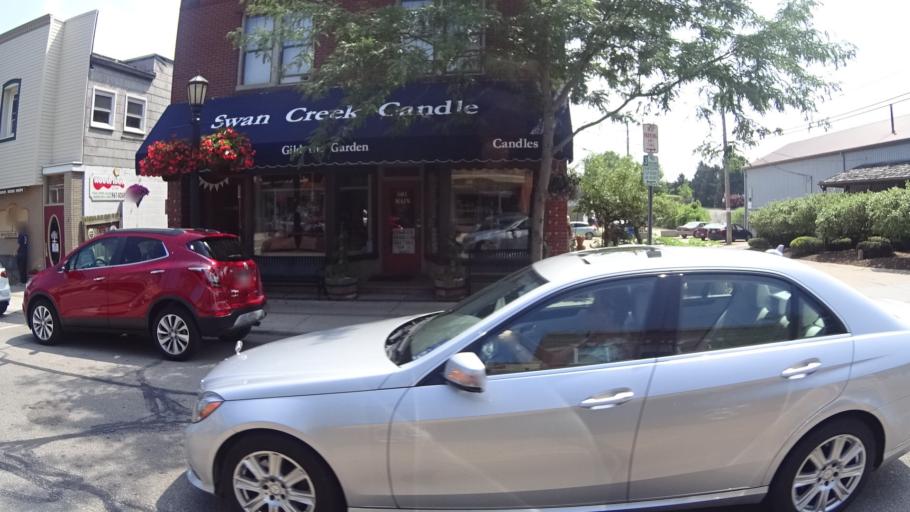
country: US
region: Ohio
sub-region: Lorain County
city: Vermilion
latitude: 41.4215
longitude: -82.3646
